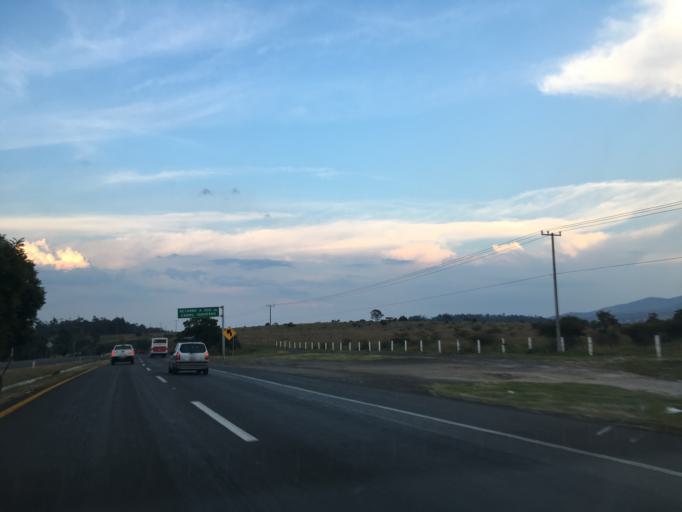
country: MX
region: Michoacan
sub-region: Morelia
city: La Mintzita (Piedra Dura)
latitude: 19.6288
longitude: -101.2758
